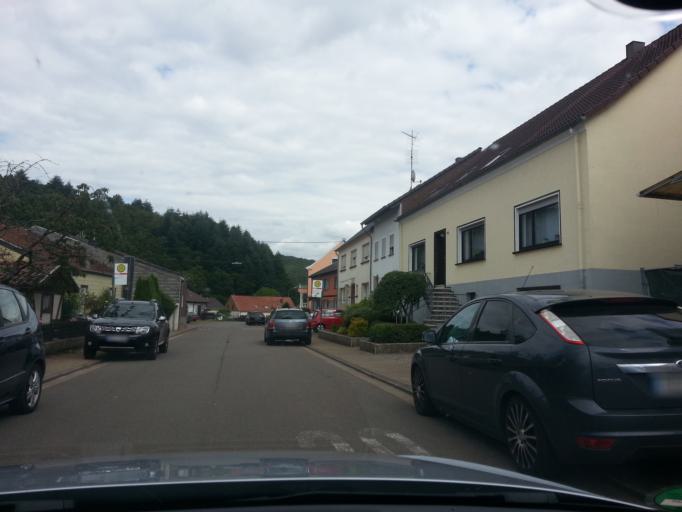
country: DE
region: Saarland
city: Nalbach
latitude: 49.4128
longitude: 6.7690
